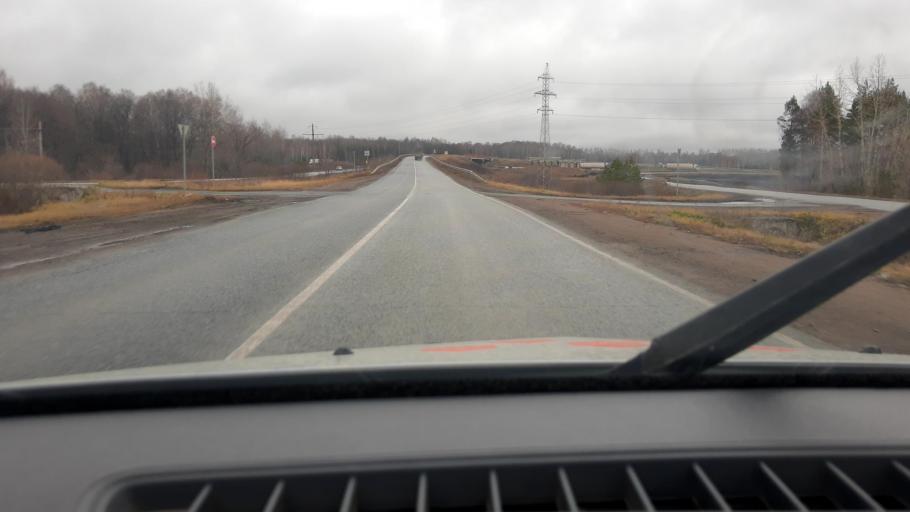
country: RU
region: Bashkortostan
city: Iglino
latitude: 54.7456
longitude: 56.2993
